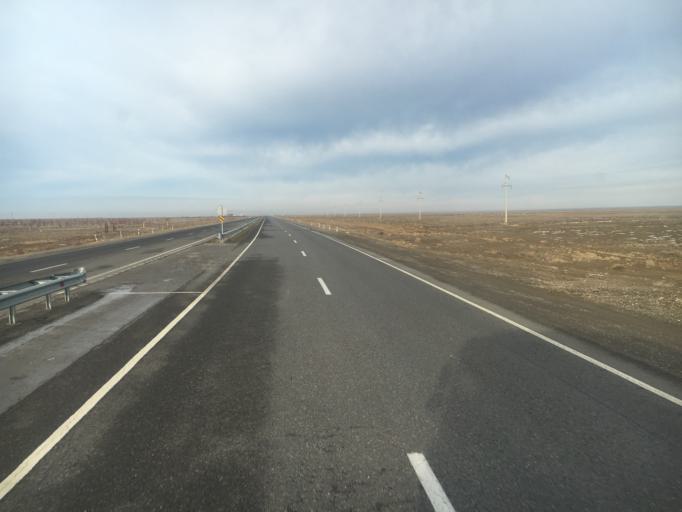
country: KZ
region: Ongtustik Qazaqstan
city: Turkestan
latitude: 43.5021
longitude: 67.8427
